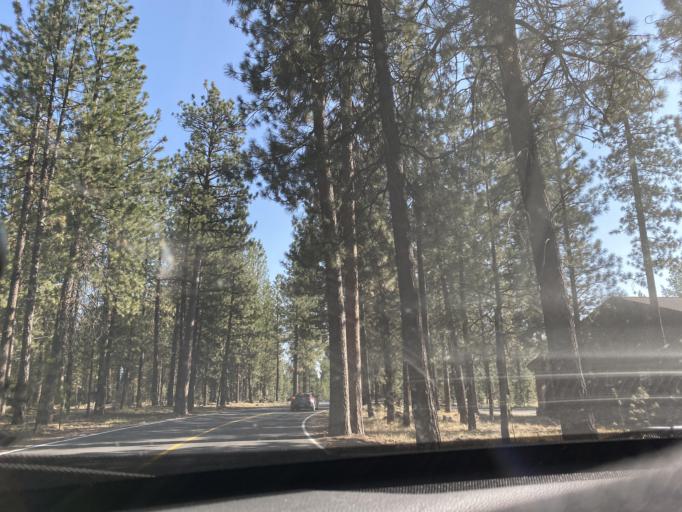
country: US
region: Oregon
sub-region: Deschutes County
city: Sunriver
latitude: 43.8879
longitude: -121.4382
